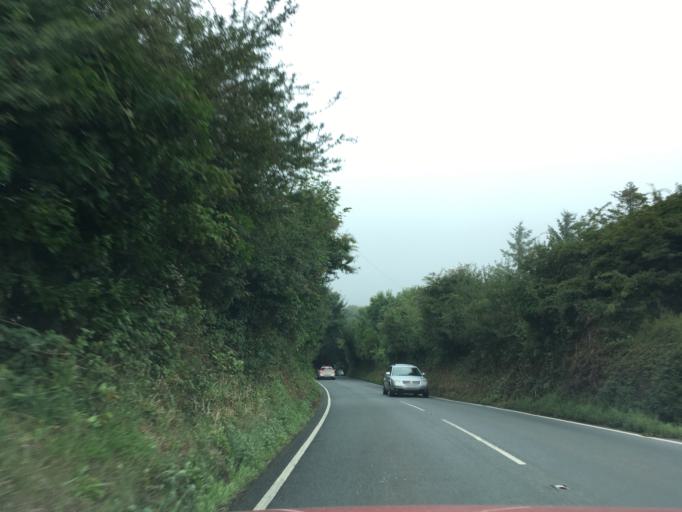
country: GB
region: Wales
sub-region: Pembrokeshire
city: Llanrhian
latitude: 51.8776
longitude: -5.1818
